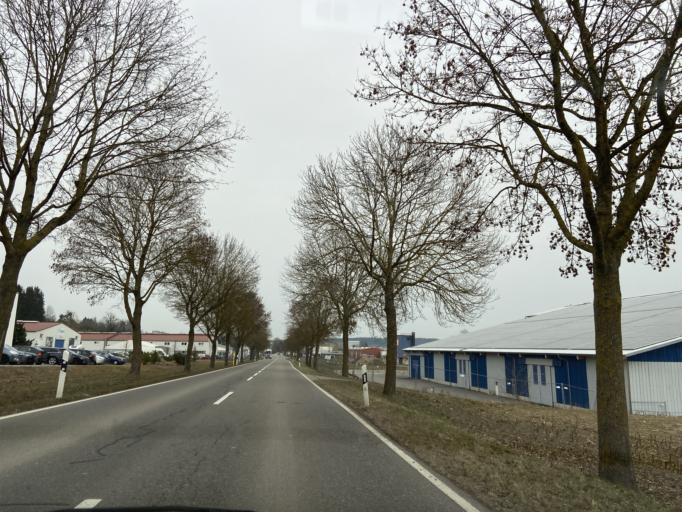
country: DE
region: Baden-Wuerttemberg
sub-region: Tuebingen Region
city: Ostrach
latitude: 47.9422
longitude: 9.3703
